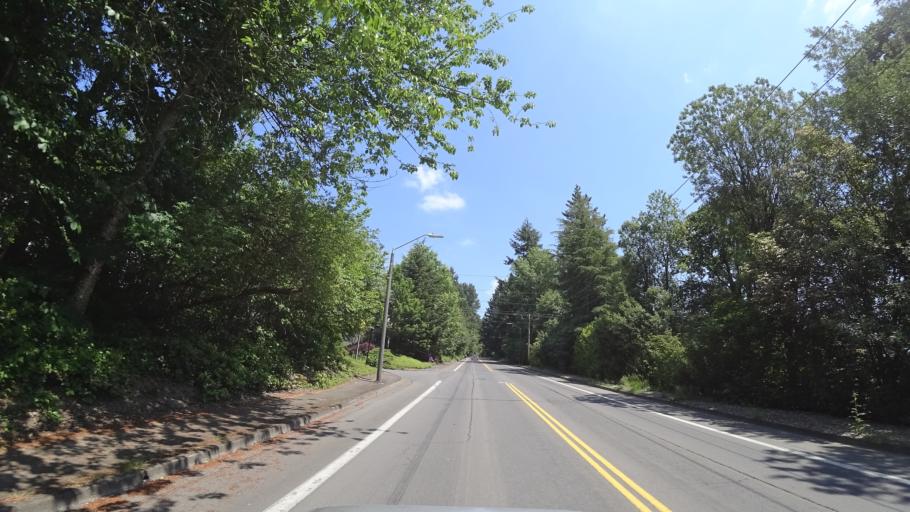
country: US
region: Oregon
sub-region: Washington County
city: Metzger
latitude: 45.4337
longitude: -122.7288
